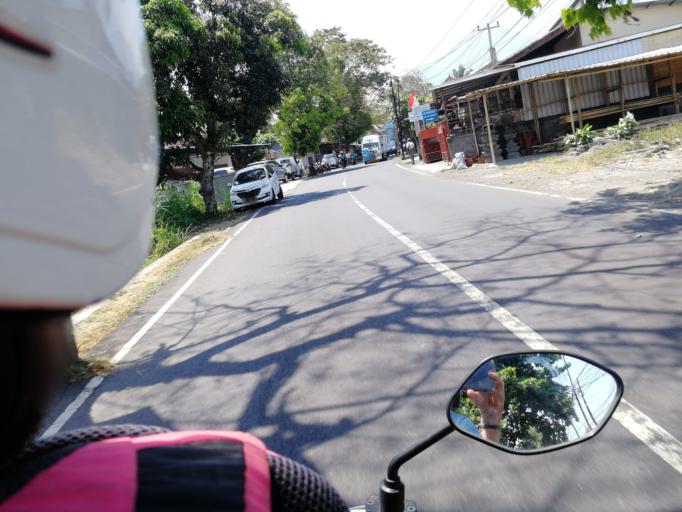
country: ID
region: Bali
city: Subagan
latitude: -8.4504
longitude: 115.5931
